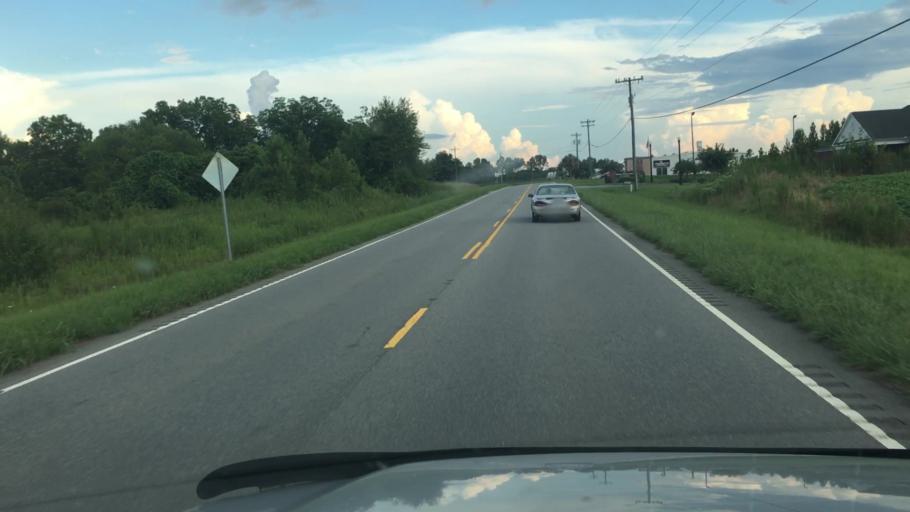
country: US
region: South Carolina
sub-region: Cherokee County
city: Gaffney
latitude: 35.1086
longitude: -81.6984
